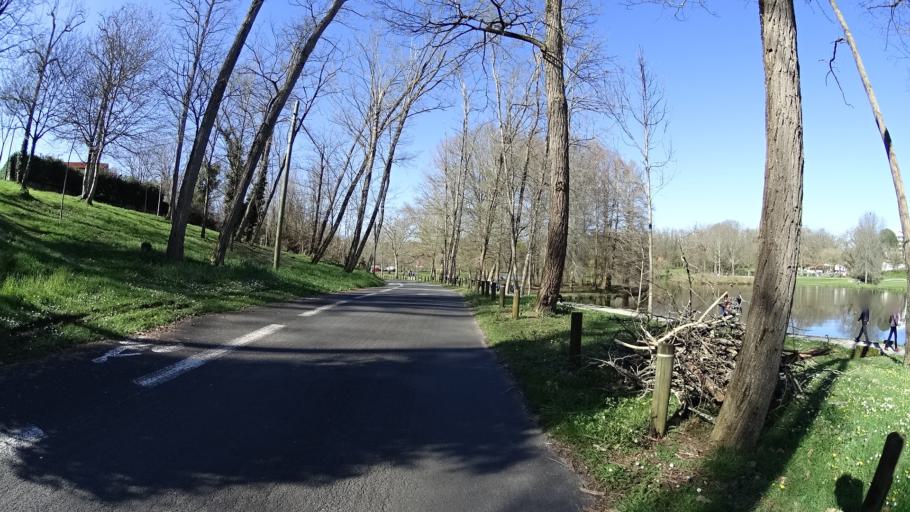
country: FR
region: Aquitaine
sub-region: Departement des Landes
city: Saint-Paul-les-Dax
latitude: 43.7303
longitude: -1.0711
